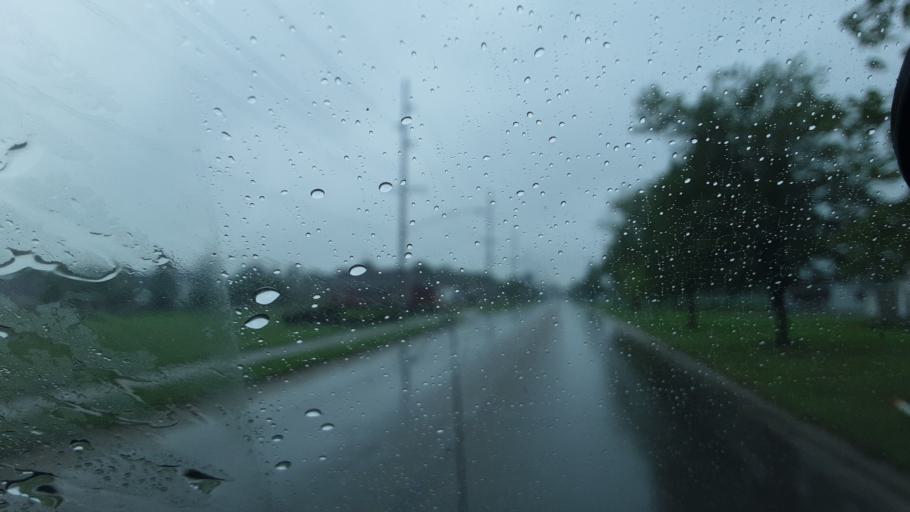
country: US
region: Indiana
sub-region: Adams County
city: Berne
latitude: 40.6497
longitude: -84.9644
